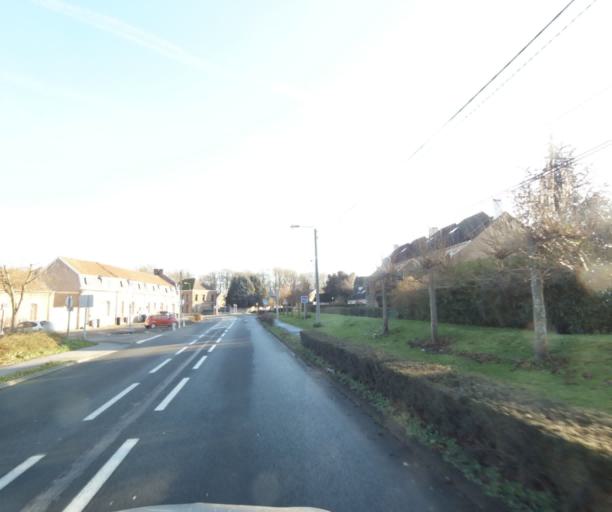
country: FR
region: Nord-Pas-de-Calais
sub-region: Departement du Nord
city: Saultain
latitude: 50.3371
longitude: 3.5734
